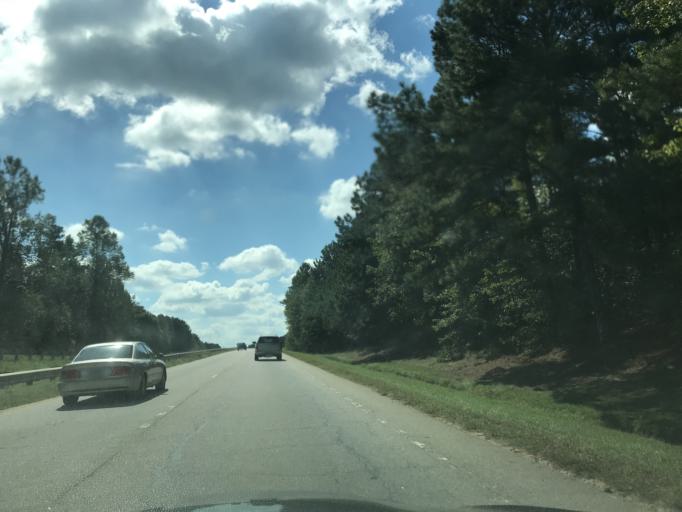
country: US
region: North Carolina
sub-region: Franklin County
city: Youngsville
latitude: 36.0644
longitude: -78.4836
